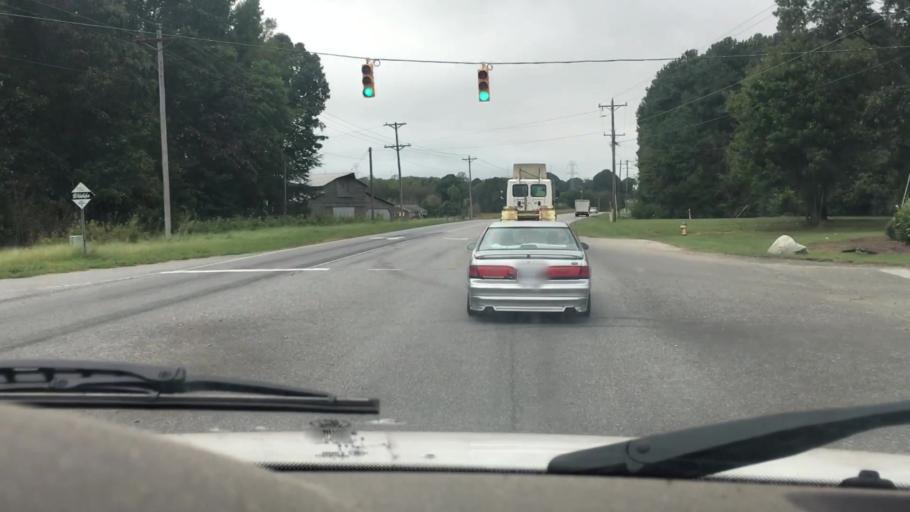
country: US
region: North Carolina
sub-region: Catawba County
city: Lake Norman of Catawba
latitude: 35.5939
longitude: -80.9654
